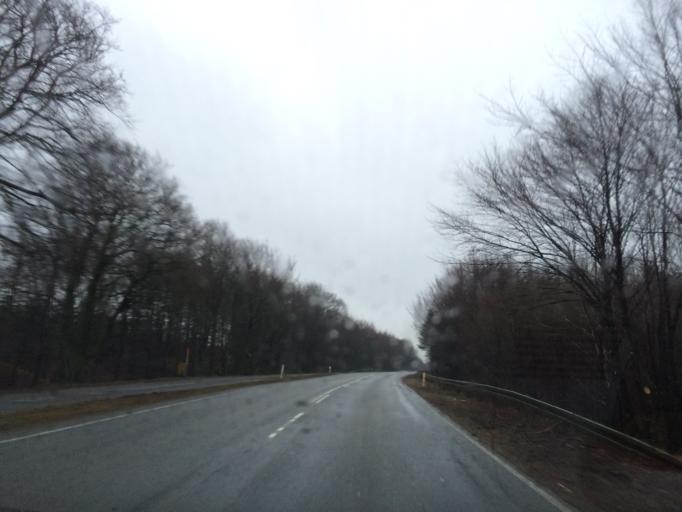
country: DK
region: North Denmark
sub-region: Mariagerfjord Kommune
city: Arden
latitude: 56.7936
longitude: 9.8212
